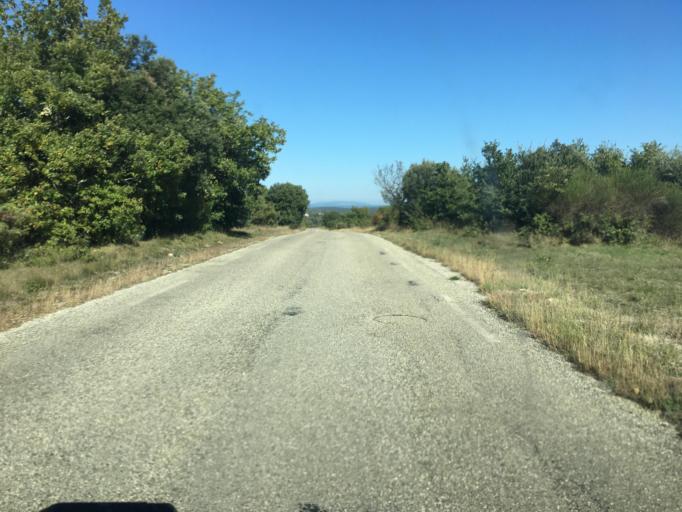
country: FR
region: Languedoc-Roussillon
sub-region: Departement du Gard
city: Barjac
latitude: 44.1738
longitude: 4.3227
